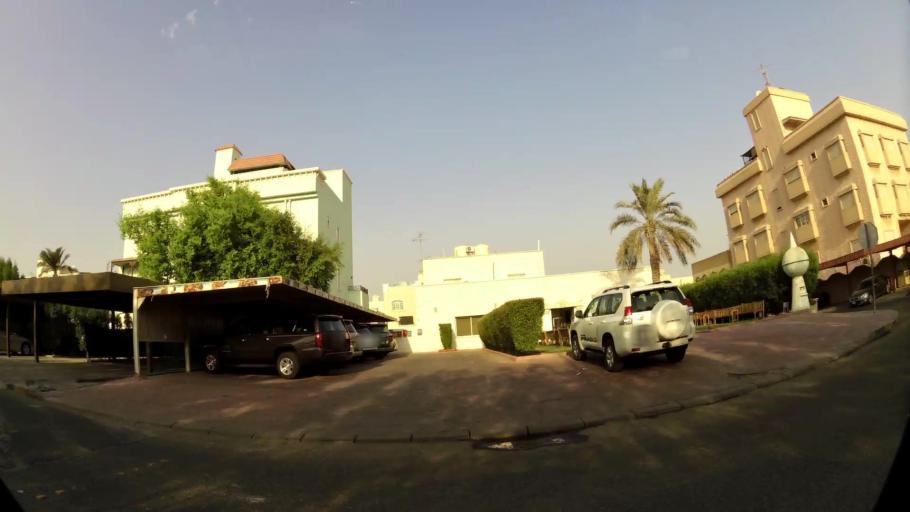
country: KW
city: Bayan
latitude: 29.3089
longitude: 48.0581
